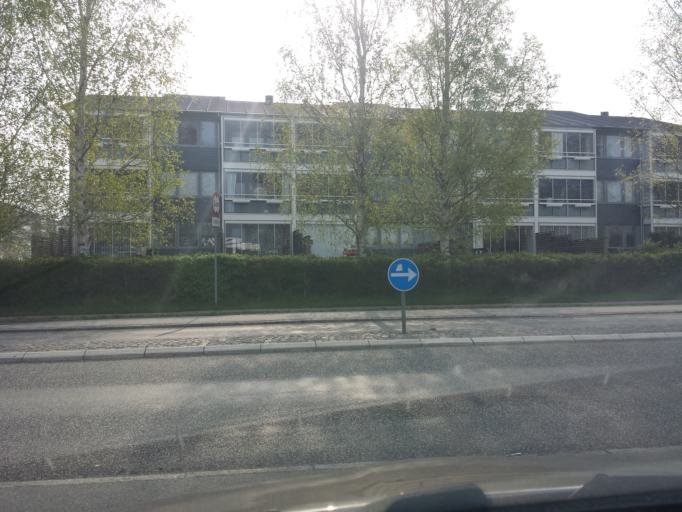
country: DK
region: Capital Region
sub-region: Ballerup Kommune
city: Ballerup
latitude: 55.7224
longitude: 12.3850
